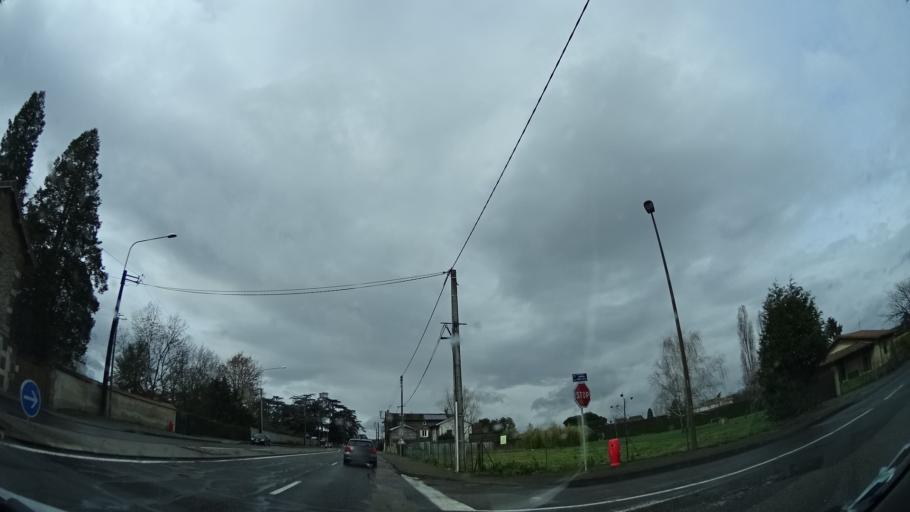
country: FR
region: Rhone-Alpes
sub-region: Departement du Rhone
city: Charbonnieres-les-Bains
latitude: 45.7883
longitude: 4.7459
